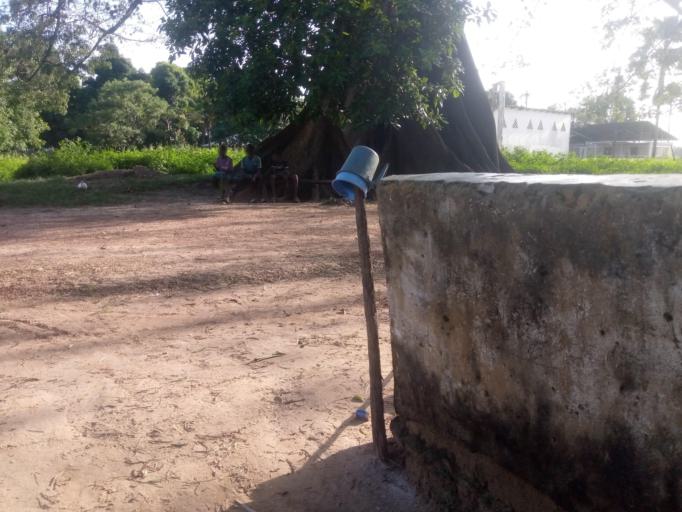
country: GM
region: Western
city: Gunjur
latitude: 13.0445
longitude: -16.7291
